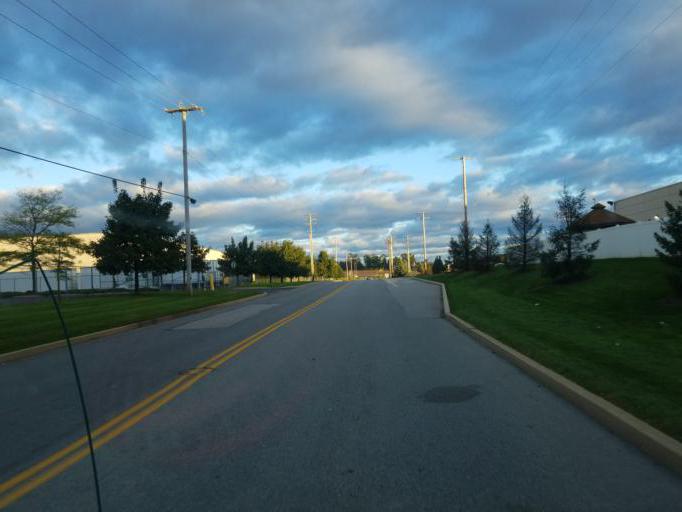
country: US
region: Pennsylvania
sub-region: York County
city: Weigelstown
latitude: 39.9322
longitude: -76.8228
